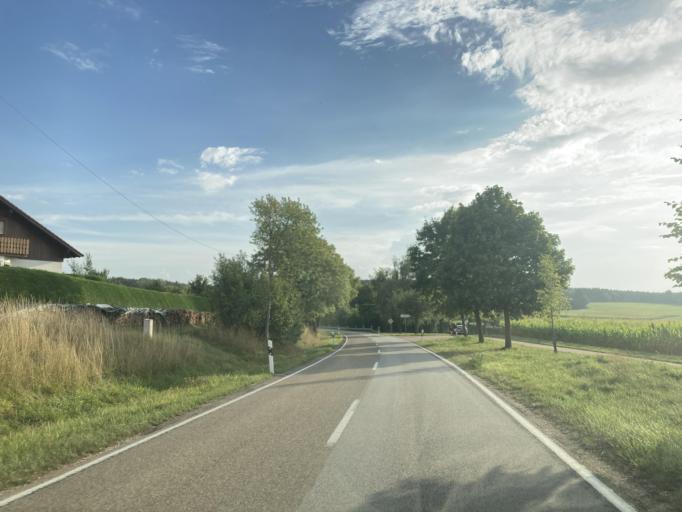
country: DE
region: Bavaria
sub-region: Swabia
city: Forheim
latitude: 48.7544
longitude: 10.4059
